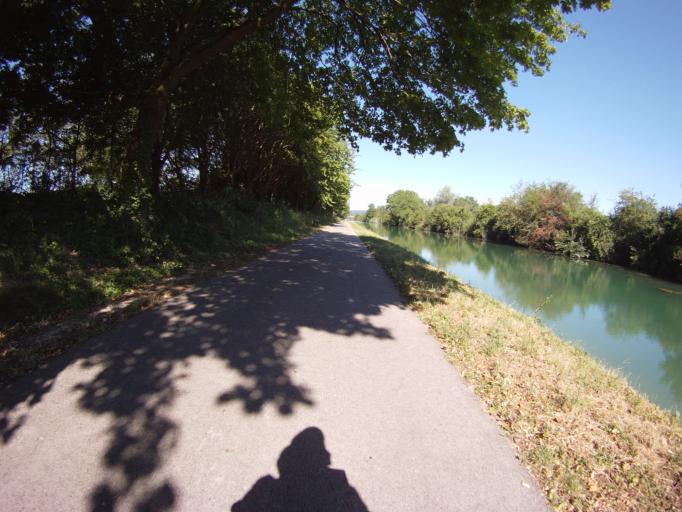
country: FR
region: Champagne-Ardenne
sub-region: Departement de la Marne
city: Magenta
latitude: 49.0570
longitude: 3.9808
